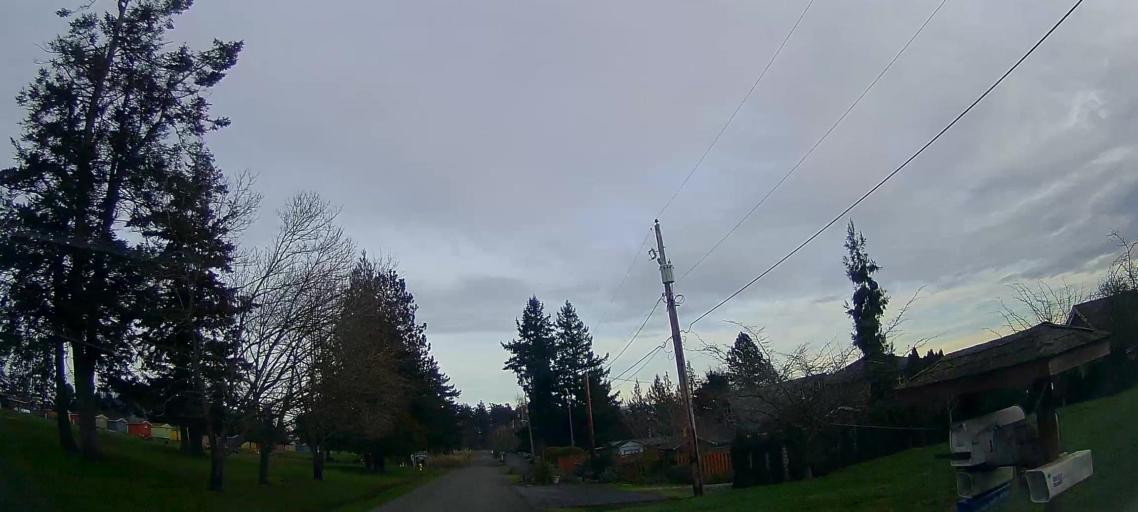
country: US
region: Washington
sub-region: Skagit County
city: Anacortes
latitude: 48.5683
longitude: -122.4957
